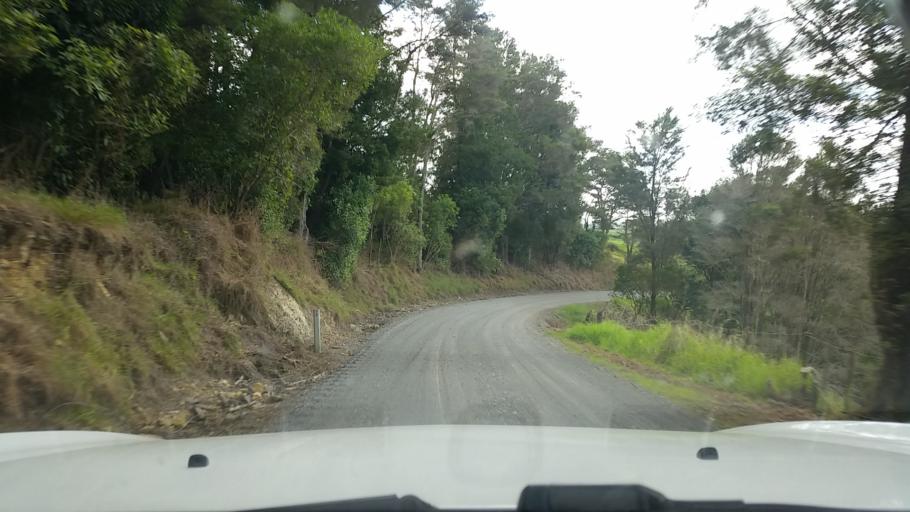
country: NZ
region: Waikato
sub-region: Hauraki District
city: Ngatea
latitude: -37.4467
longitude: 175.4851
